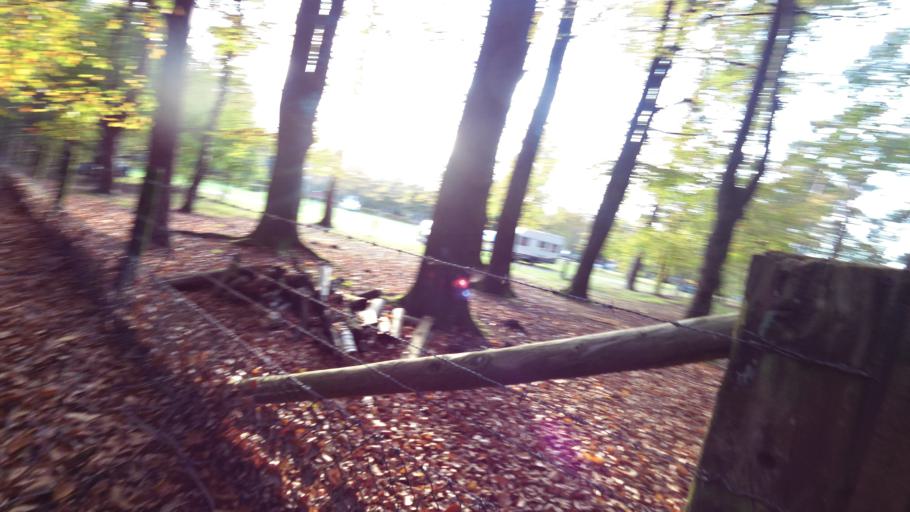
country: NL
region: Gelderland
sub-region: Gemeente Apeldoorn
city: Uddel
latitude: 52.2784
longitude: 5.8103
